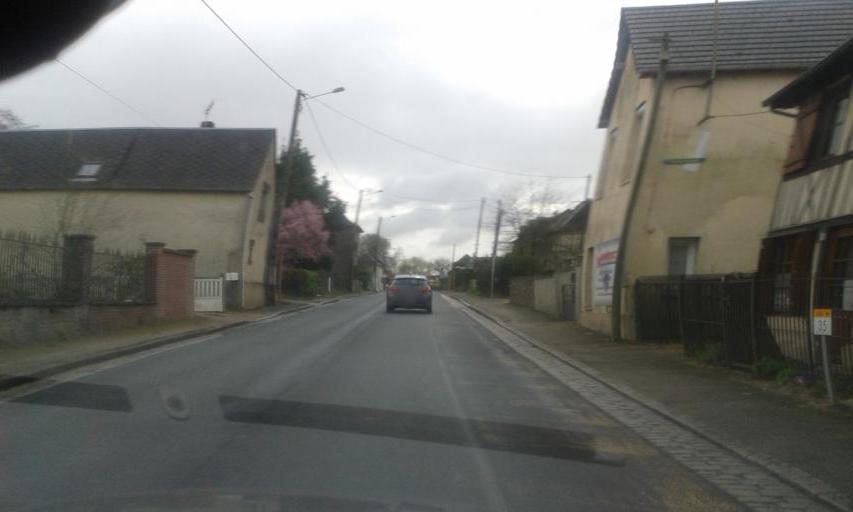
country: FR
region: Haute-Normandie
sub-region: Departement de l'Eure
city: Fleury-sur-Andelle
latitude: 49.3860
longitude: 1.3090
